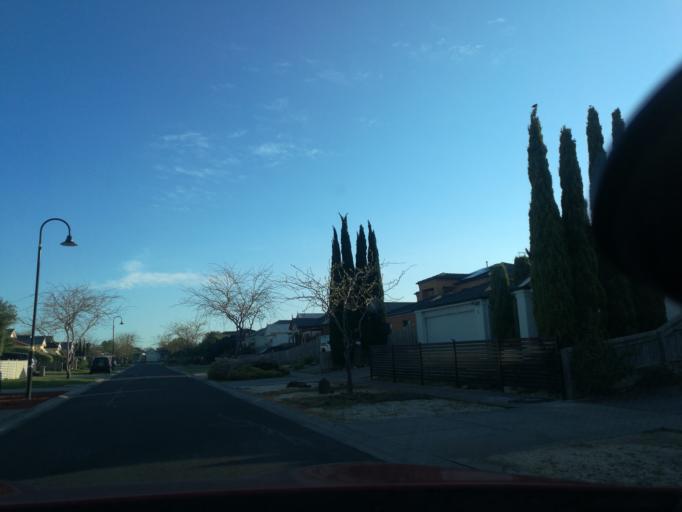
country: AU
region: Victoria
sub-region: Wyndham
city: Williams Landing
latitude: -37.8829
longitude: 144.7428
